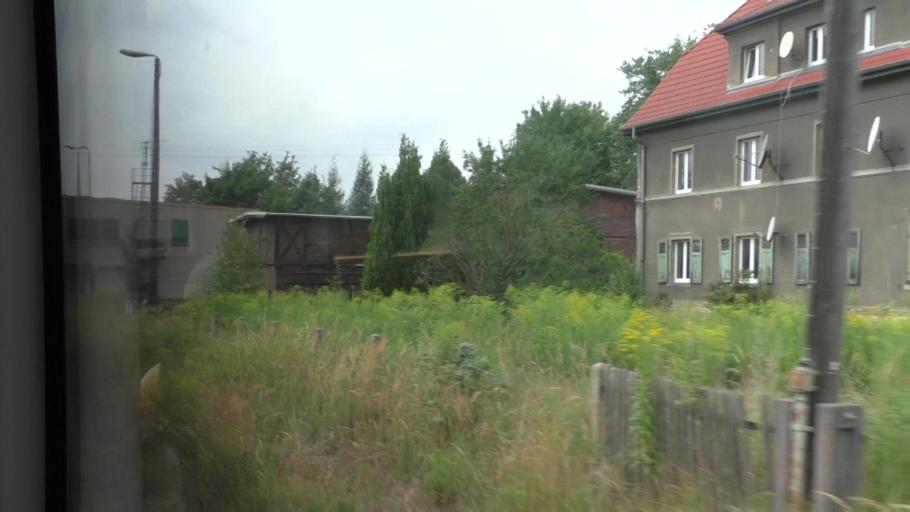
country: DE
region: Saxony
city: Hirschfelde
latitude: 50.9396
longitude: 14.8830
